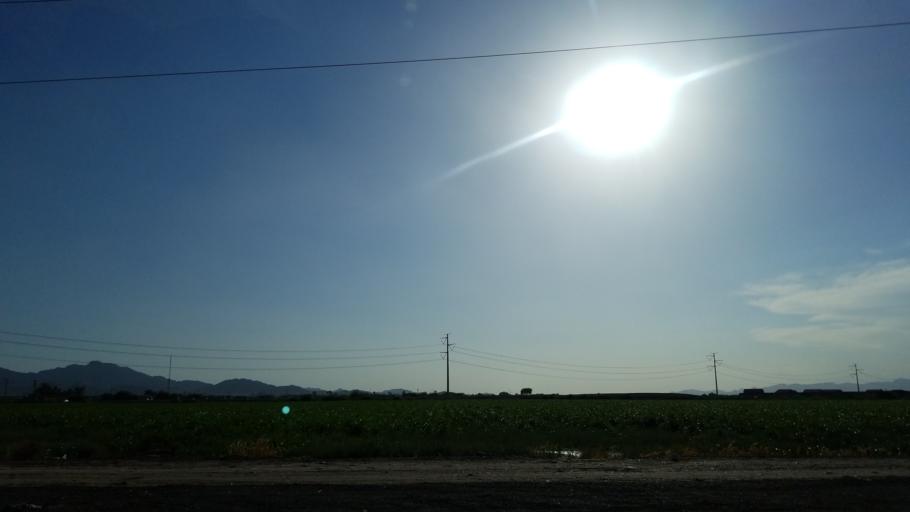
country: US
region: Arizona
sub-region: Maricopa County
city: Laveen
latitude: 33.3794
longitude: -112.2198
